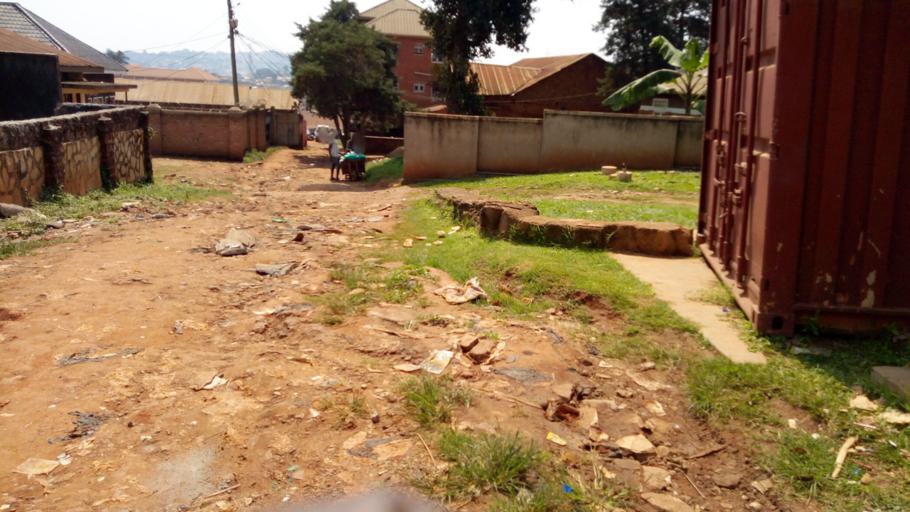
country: UG
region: Central Region
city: Kampala Central Division
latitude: 0.3444
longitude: 32.5678
